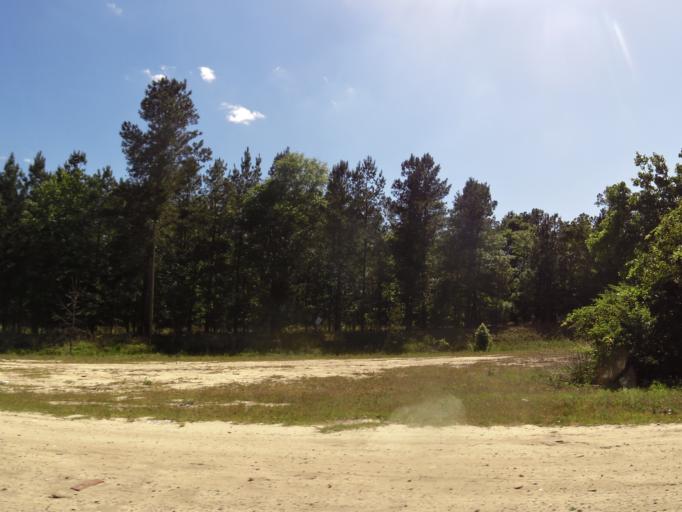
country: US
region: South Carolina
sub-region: Barnwell County
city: Williston
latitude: 33.4165
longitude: -81.4748
